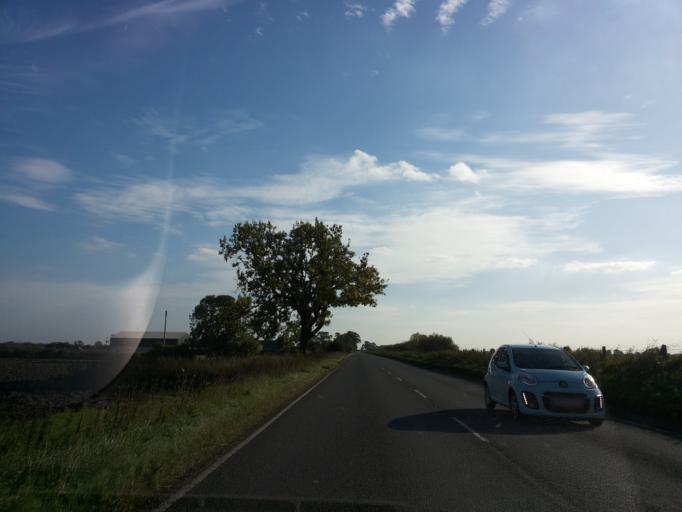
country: GB
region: England
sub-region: East Riding of Yorkshire
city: Rawcliffe
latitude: 53.6684
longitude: -0.9905
